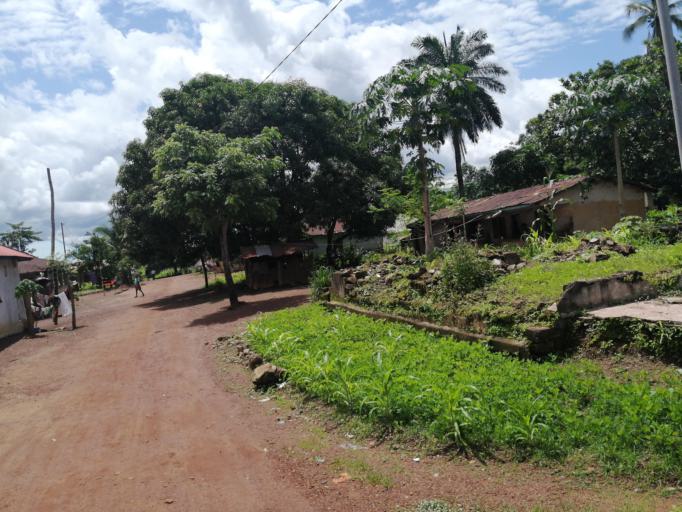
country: SL
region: Northern Province
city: Port Loko
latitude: 8.7675
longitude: -12.7832
